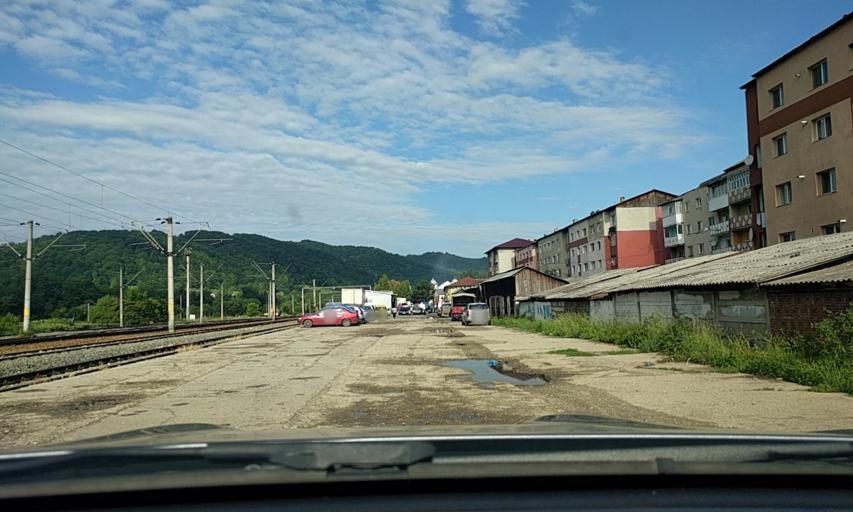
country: RO
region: Bistrita-Nasaud
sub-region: Oras Nasaud
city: Nasaud
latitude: 47.2815
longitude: 24.4142
